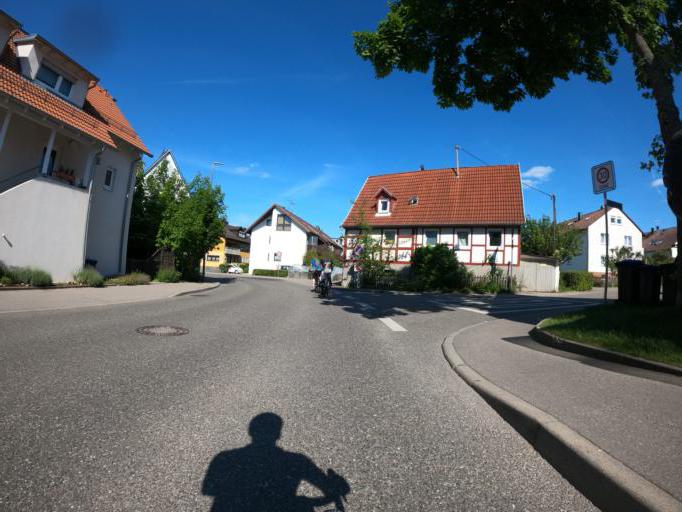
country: DE
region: Baden-Wuerttemberg
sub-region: Regierungsbezirk Stuttgart
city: Magstadt
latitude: 48.7629
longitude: 8.9904
